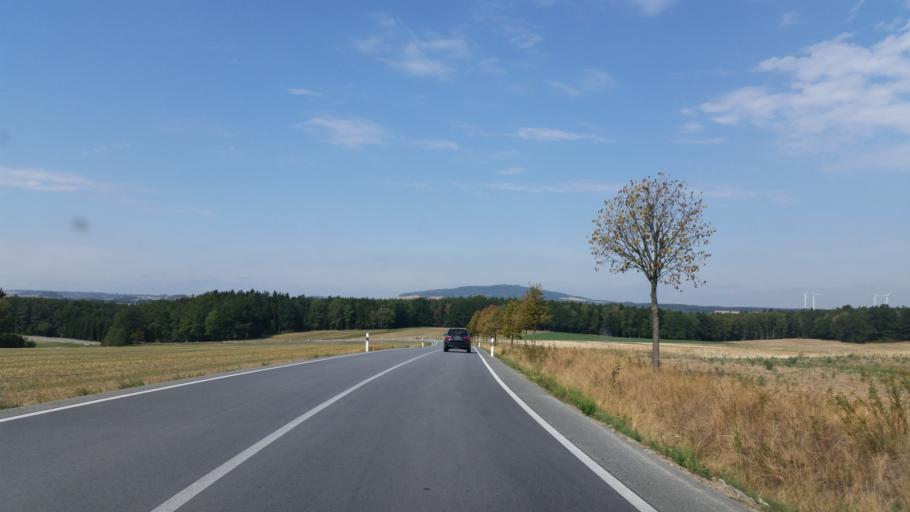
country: DE
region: Saxony
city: Grosshennersdorf
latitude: 50.9806
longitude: 14.7653
